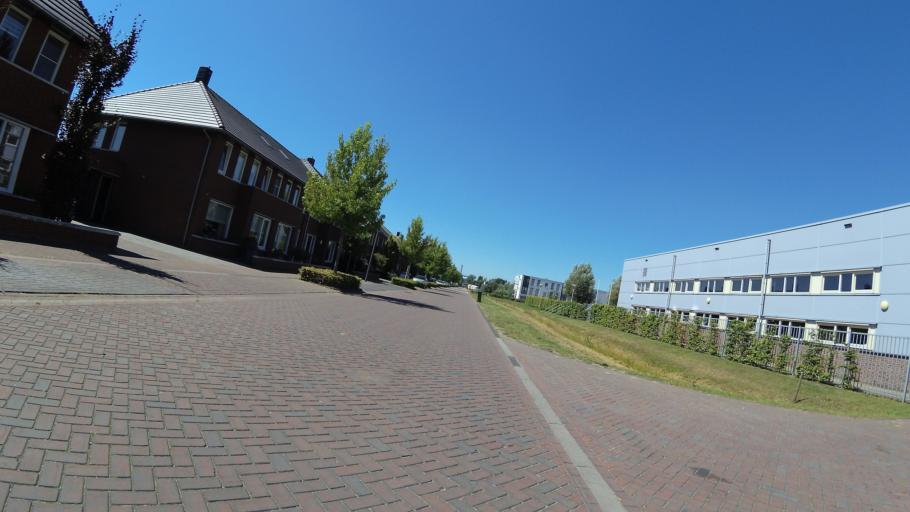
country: NL
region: North Brabant
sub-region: Gemeente Waalwijk
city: Waalwijk
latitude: 51.6734
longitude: 5.0498
